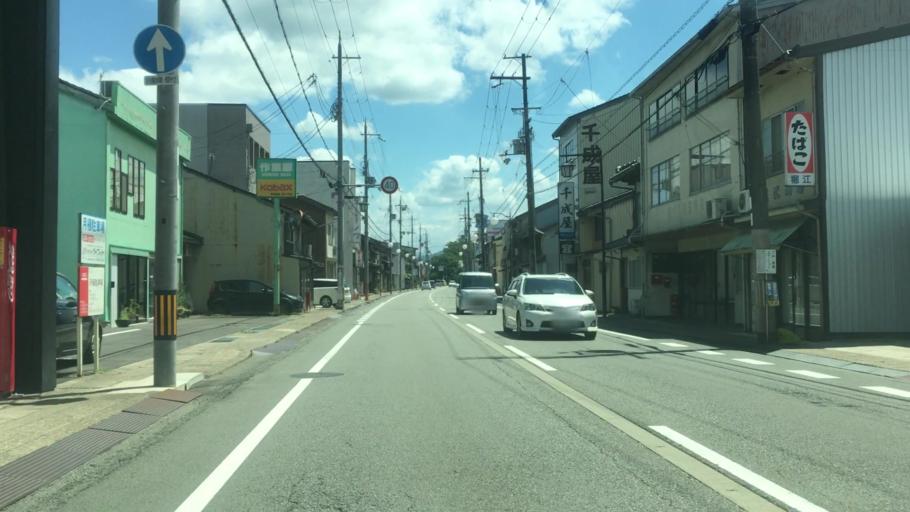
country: JP
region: Hyogo
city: Toyooka
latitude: 35.5377
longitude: 134.8249
